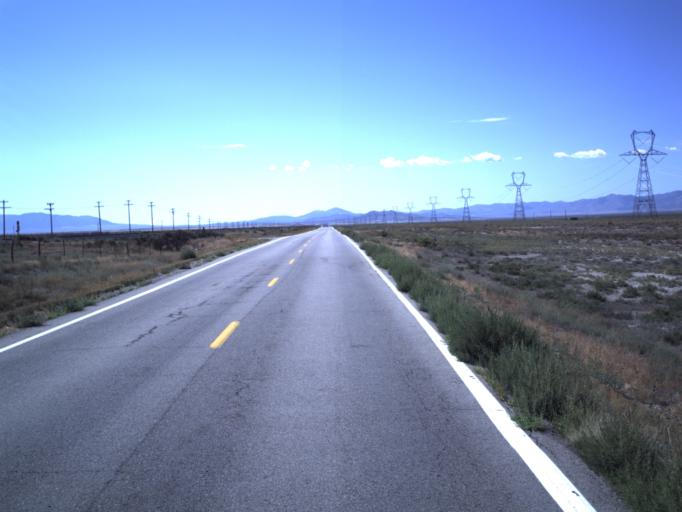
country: US
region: Utah
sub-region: Tooele County
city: Tooele
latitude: 40.3218
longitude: -112.4066
